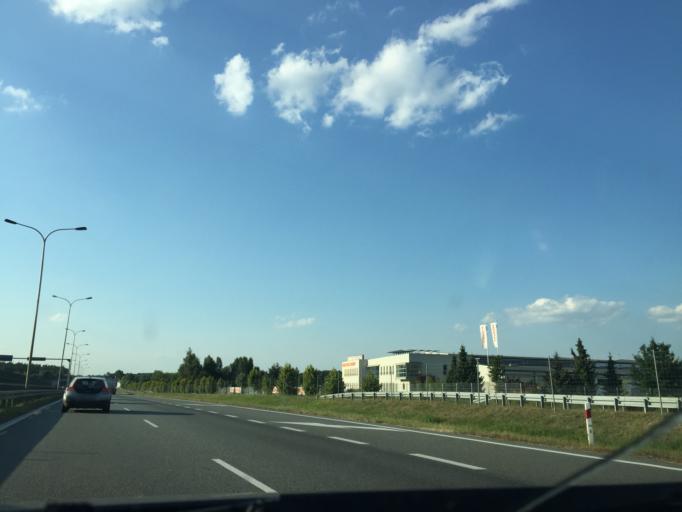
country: PL
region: Masovian Voivodeship
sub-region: Powiat bialobrzeski
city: Sucha
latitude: 51.6114
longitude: 20.9813
